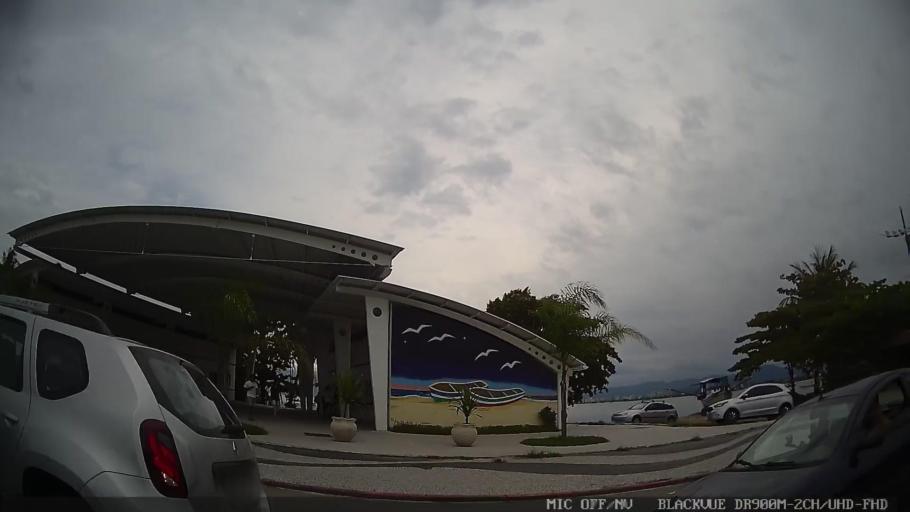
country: BR
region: Sao Paulo
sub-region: Caraguatatuba
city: Caraguatatuba
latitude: -23.6239
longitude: -45.3984
